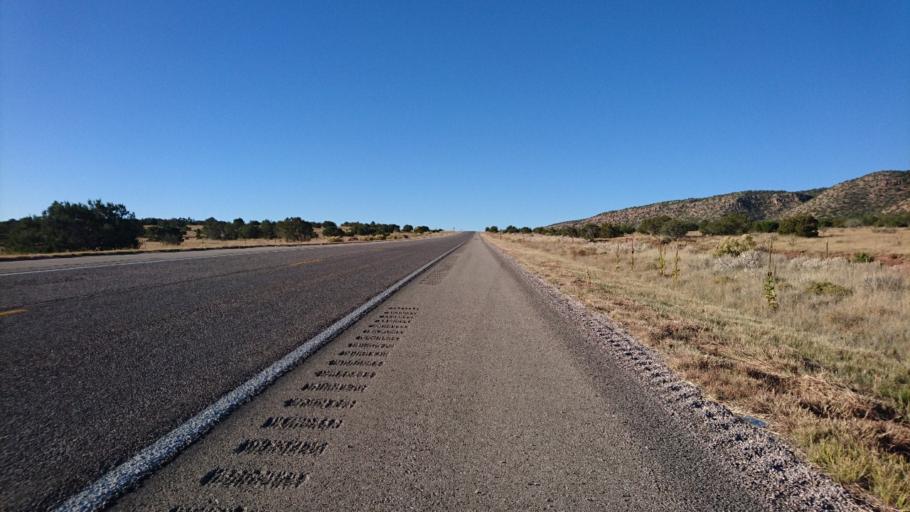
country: US
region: New Mexico
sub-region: Cibola County
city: Grants
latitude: 35.0045
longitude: -107.8930
